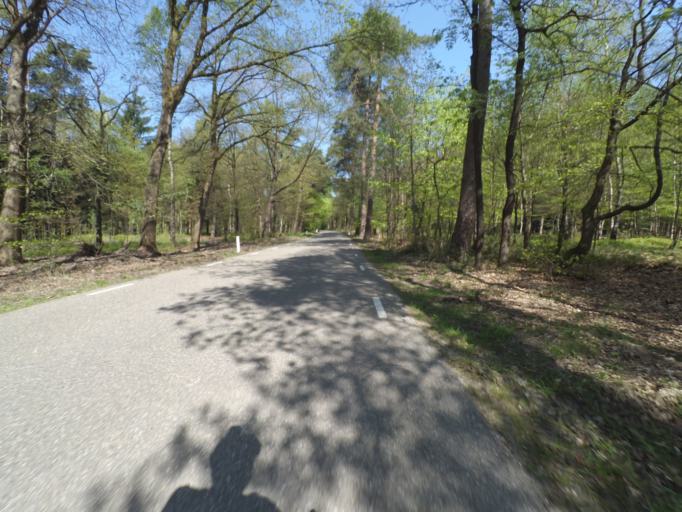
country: NL
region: Gelderland
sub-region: Gemeente Apeldoorn
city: Apeldoorn
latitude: 52.2238
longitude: 5.8781
